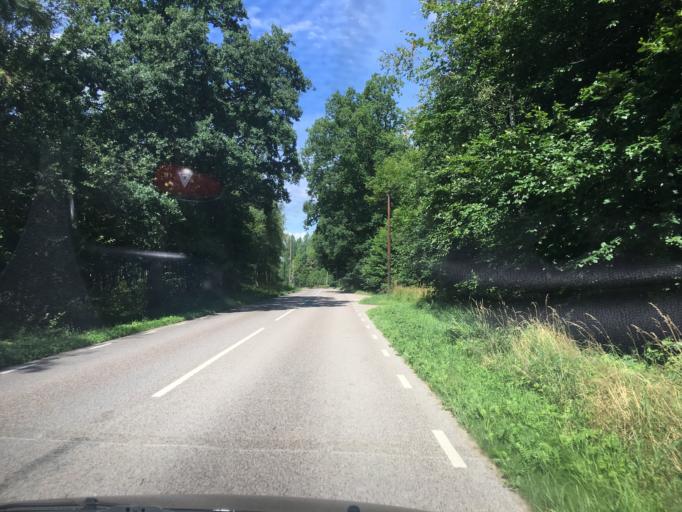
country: SE
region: Skane
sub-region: Svalovs Kommun
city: Kagerod
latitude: 55.9899
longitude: 13.1022
